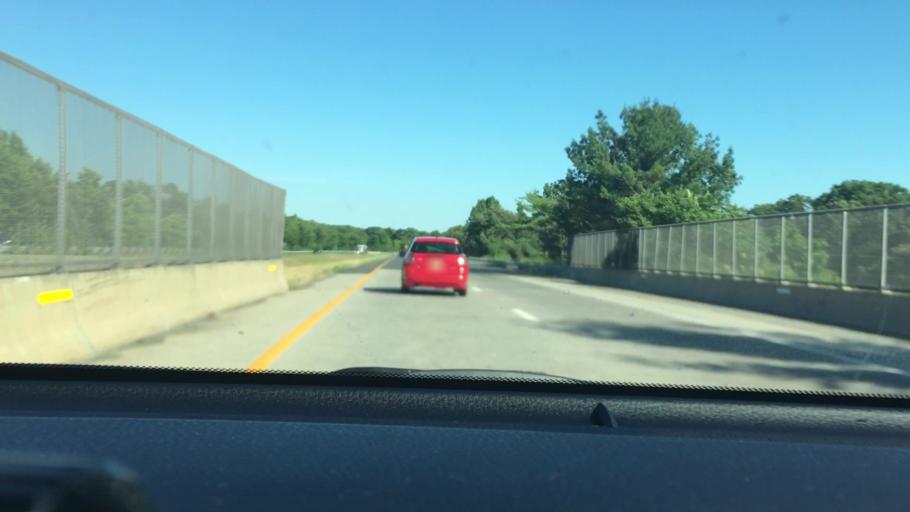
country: US
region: New Jersey
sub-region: Gloucester County
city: Clayton
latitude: 39.6036
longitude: -75.0799
